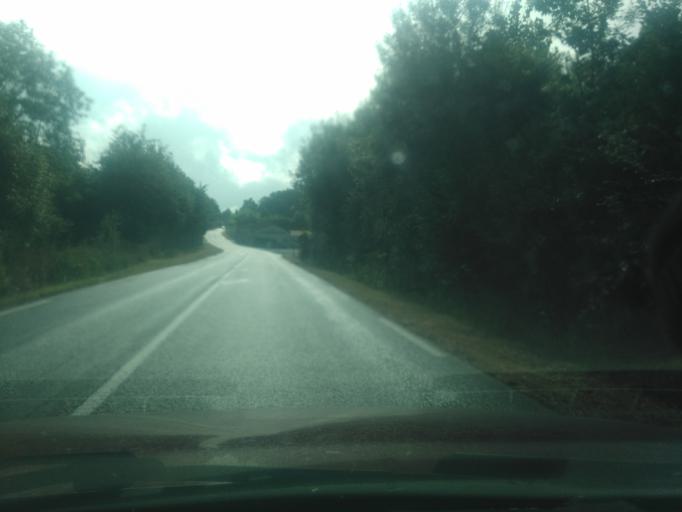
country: FR
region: Poitou-Charentes
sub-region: Departement des Deux-Sevres
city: Le Tallud
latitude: 46.6256
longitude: -0.3244
